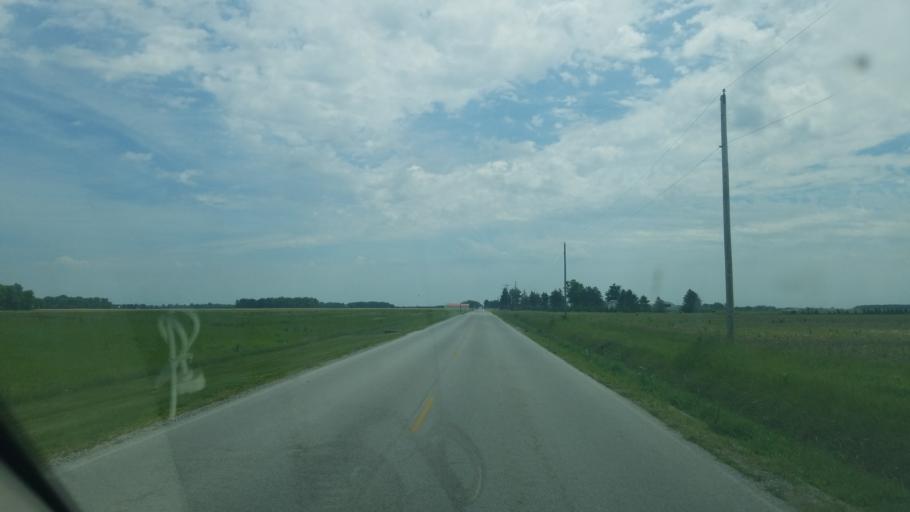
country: US
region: Ohio
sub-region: Wood County
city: Bowling Green
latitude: 41.2967
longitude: -83.6249
